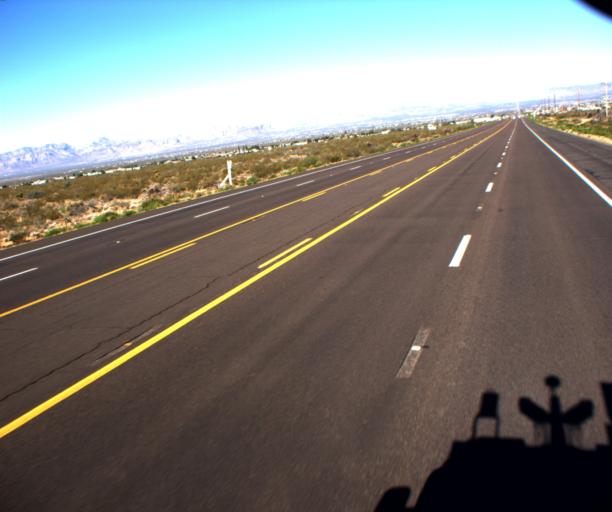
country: US
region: Arizona
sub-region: Mohave County
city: Golden Valley
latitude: 35.2193
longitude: -114.1588
